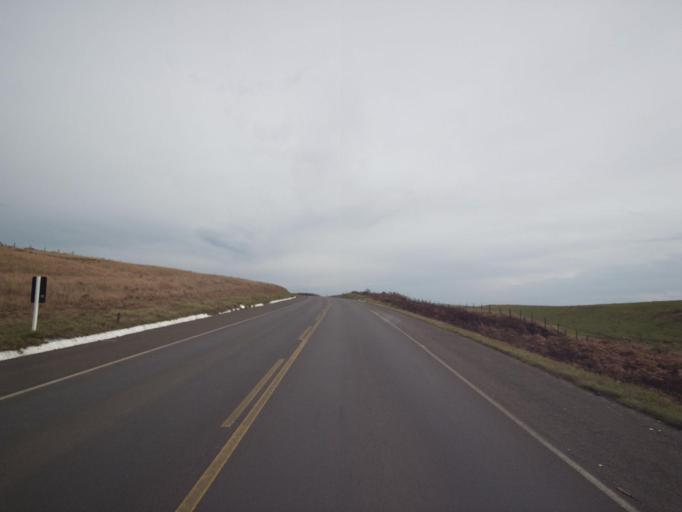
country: BR
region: Parana
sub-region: Palmas
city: Palmas
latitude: -26.7288
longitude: -51.6395
